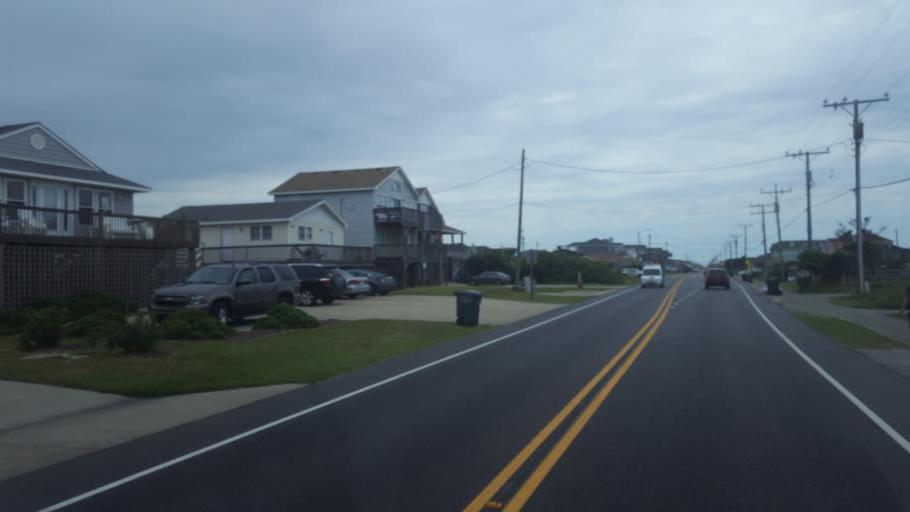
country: US
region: North Carolina
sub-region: Dare County
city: Nags Head
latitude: 35.9809
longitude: -75.6375
